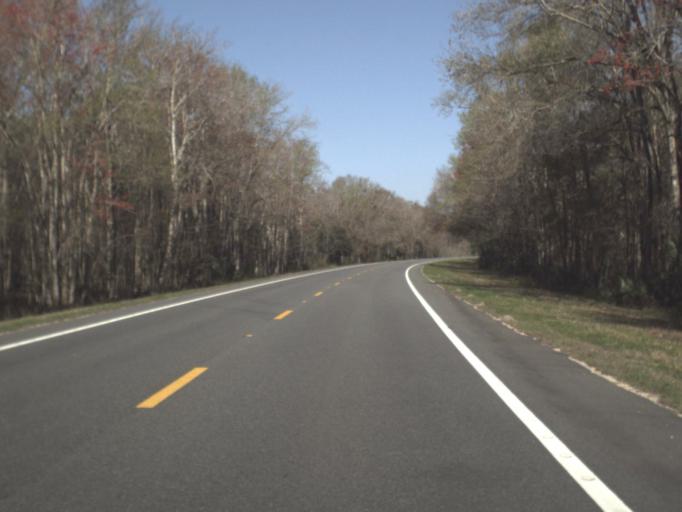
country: US
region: Florida
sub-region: Leon County
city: Woodville
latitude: 30.1578
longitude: -83.9978
